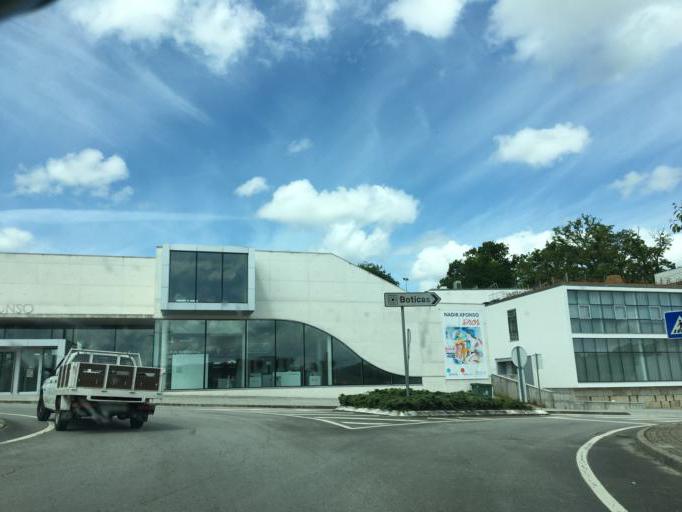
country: PT
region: Vila Real
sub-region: Boticas
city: Boticas
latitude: 41.6862
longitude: -7.6679
